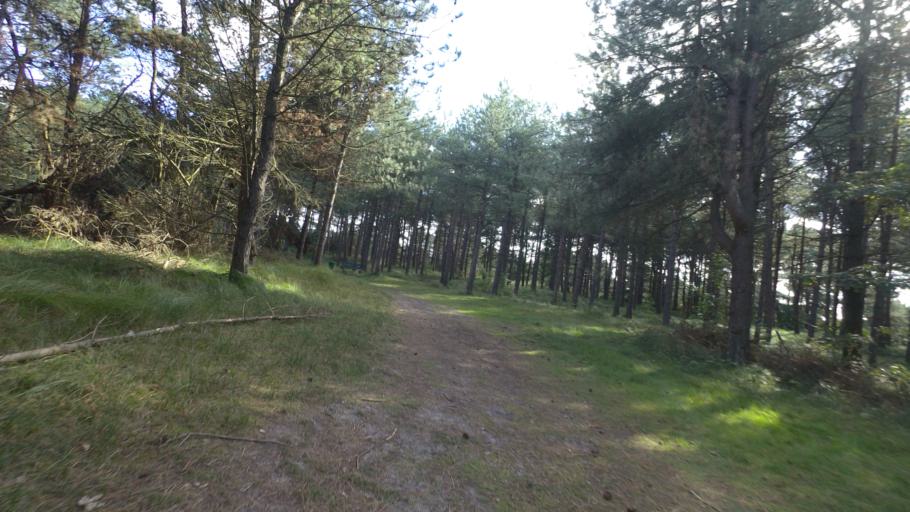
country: NL
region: Friesland
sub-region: Gemeente Ameland
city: Nes
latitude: 53.4592
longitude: 5.8183
